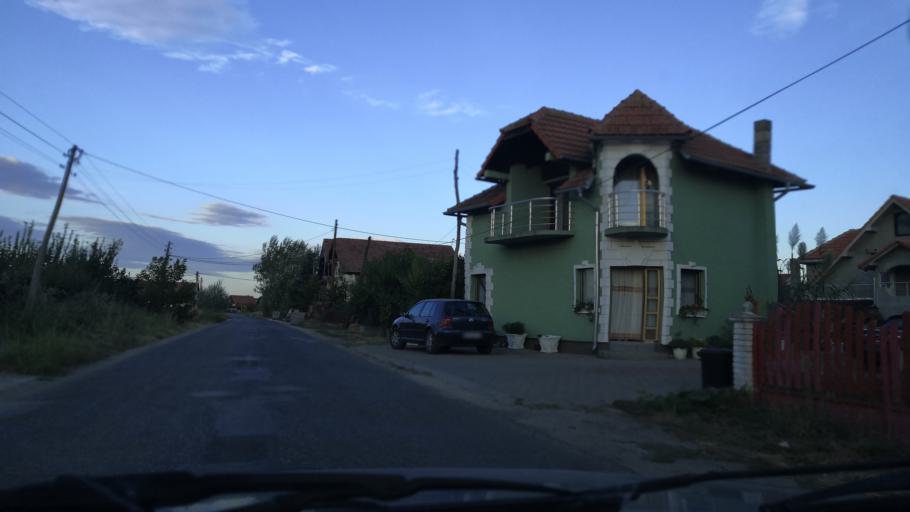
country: RS
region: Central Serbia
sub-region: Borski Okrug
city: Negotin
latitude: 44.2350
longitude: 22.5446
